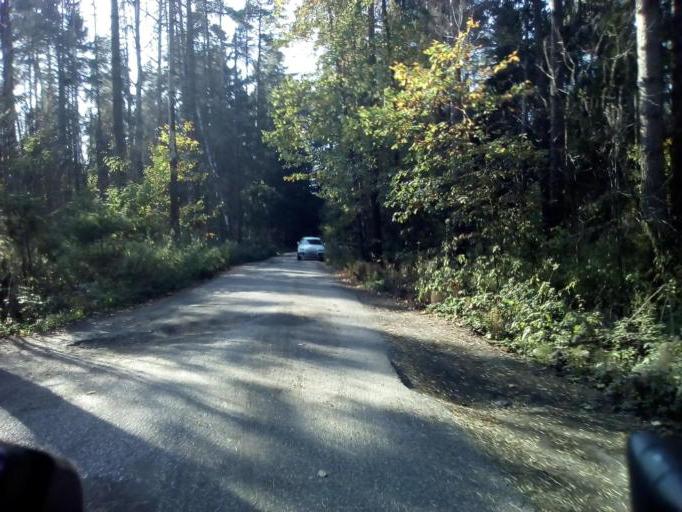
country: RU
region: Moskovskaya
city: Malyshevo
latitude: 55.5554
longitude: 38.3346
